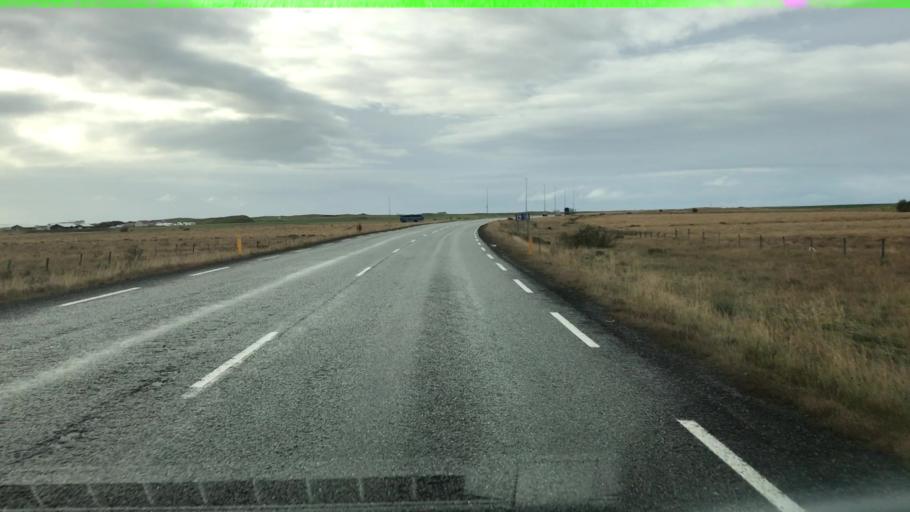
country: IS
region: West
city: Akranes
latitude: 64.3092
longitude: -21.9828
